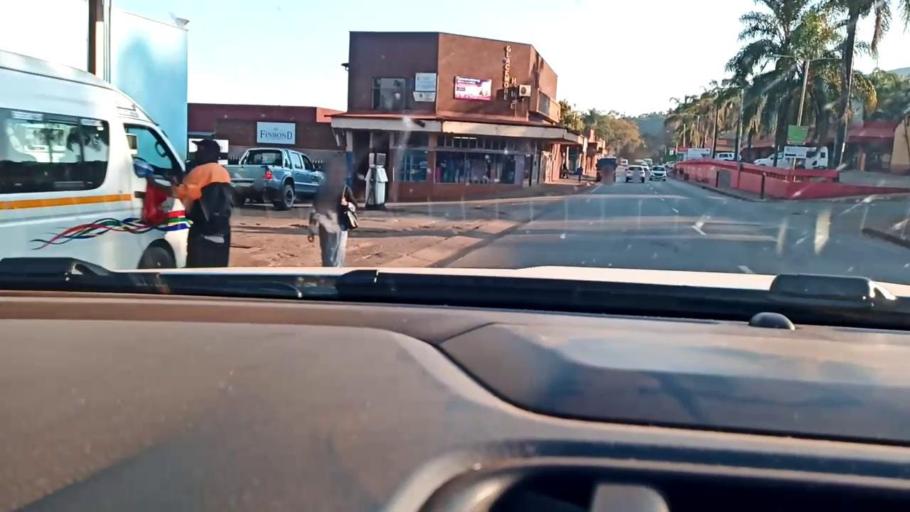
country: ZA
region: Limpopo
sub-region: Mopani District Municipality
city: Duiwelskloof
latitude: -23.6967
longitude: 30.1398
